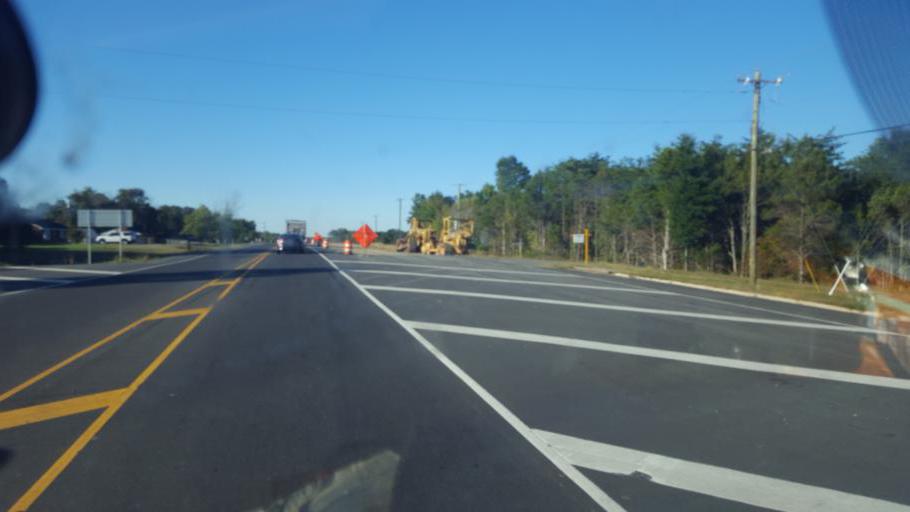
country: US
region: Virginia
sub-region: Prince William County
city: Nokesville
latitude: 38.7204
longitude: -77.5574
